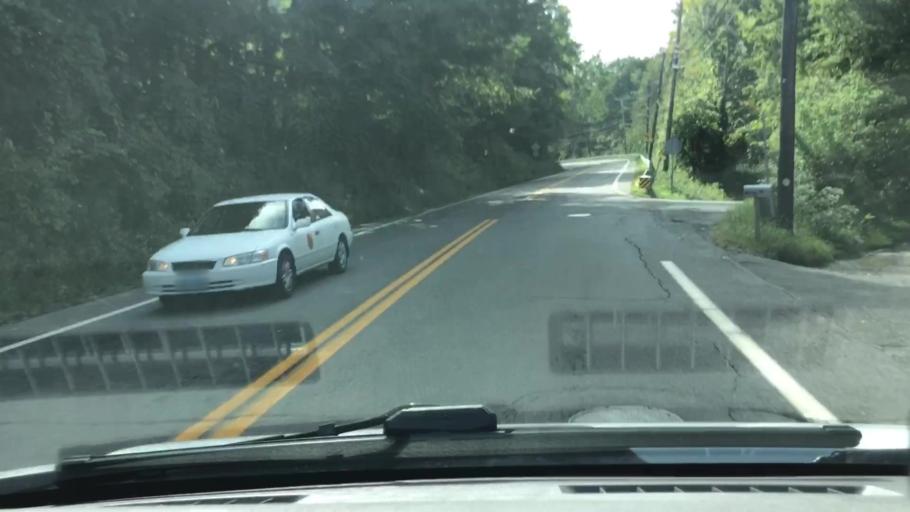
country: US
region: Massachusetts
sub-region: Berkshire County
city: North Adams
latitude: 42.6927
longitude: -73.0863
